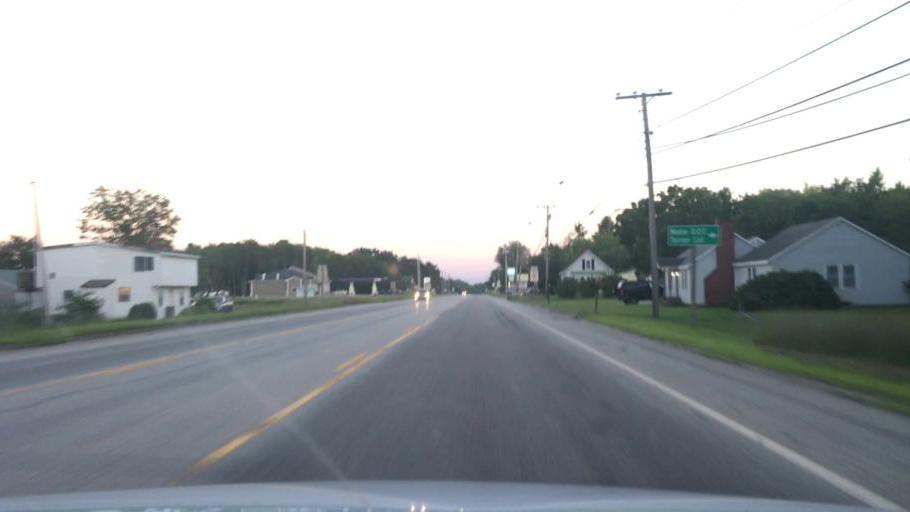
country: US
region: Maine
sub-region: Androscoggin County
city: Turner
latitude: 44.1907
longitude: -70.2389
